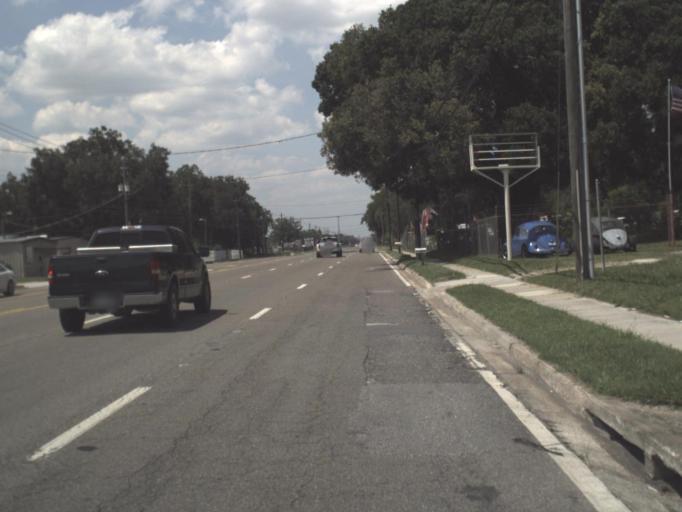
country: US
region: Florida
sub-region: Hillsborough County
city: Palm River-Clair Mel
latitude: 27.9292
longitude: -82.4018
